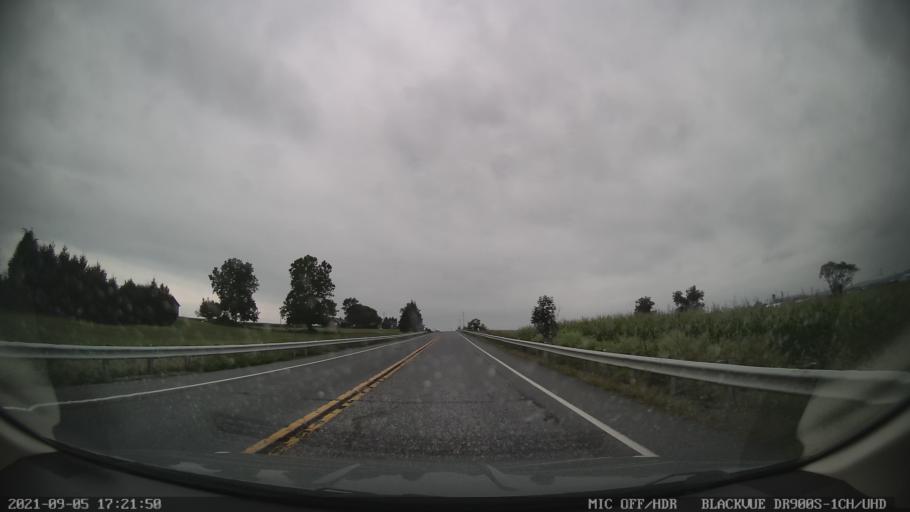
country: US
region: Pennsylvania
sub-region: Berks County
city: Kutztown
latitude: 40.4775
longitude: -75.7783
